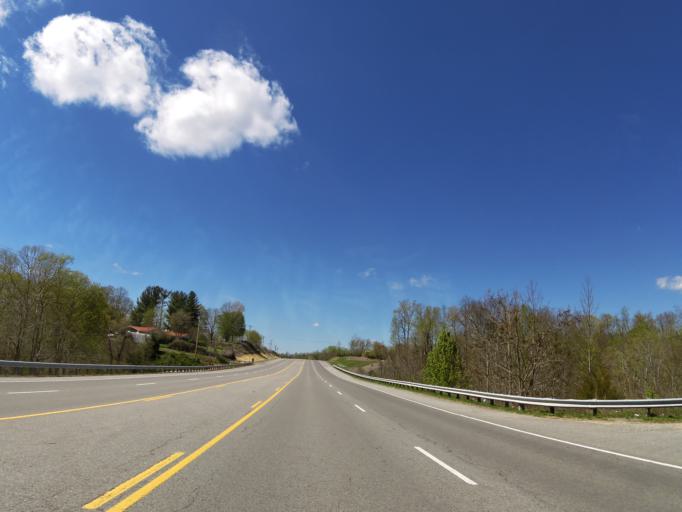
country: US
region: Tennessee
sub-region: DeKalb County
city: Smithville
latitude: 35.9831
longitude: -85.8709
